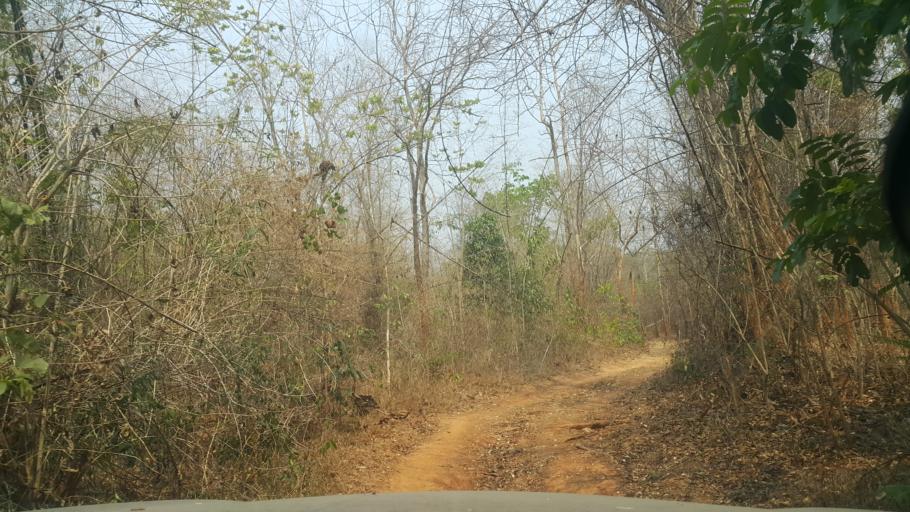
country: TH
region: Lampang
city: Sop Prap
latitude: 17.8065
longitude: 99.2520
